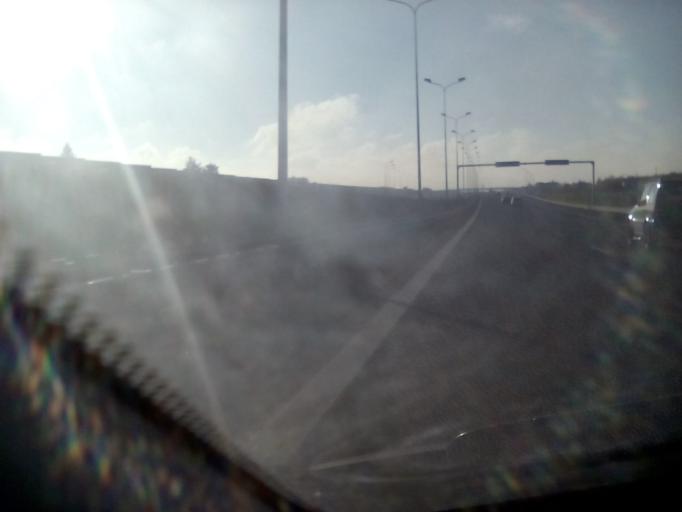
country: PL
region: Masovian Voivodeship
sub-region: Powiat grojecki
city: Grojec
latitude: 51.8382
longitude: 20.8760
